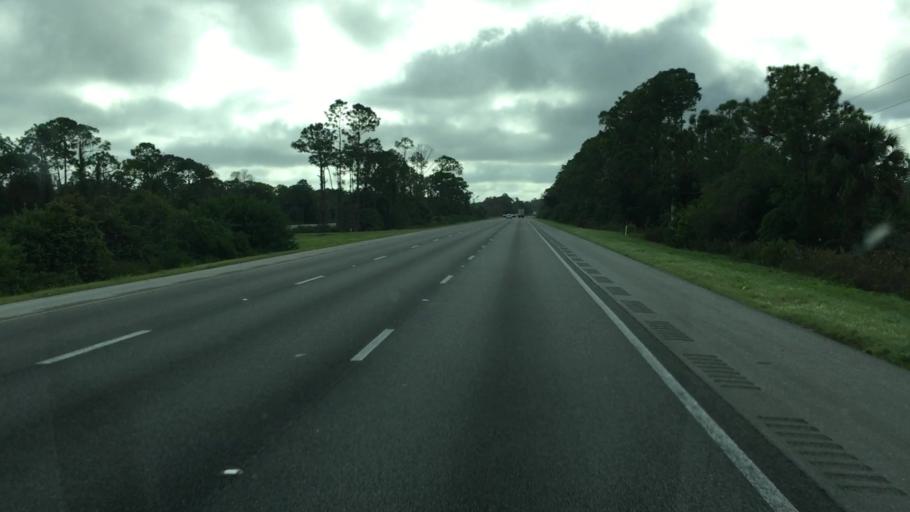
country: US
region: Florida
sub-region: Volusia County
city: Samsula-Spruce Creek
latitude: 29.0750
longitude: -81.0137
